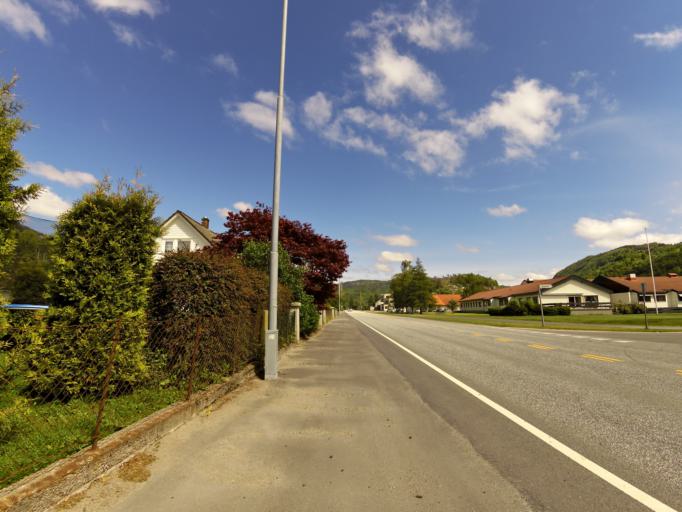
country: NO
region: Vest-Agder
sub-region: Kvinesdal
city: Liknes
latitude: 58.3088
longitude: 6.9574
